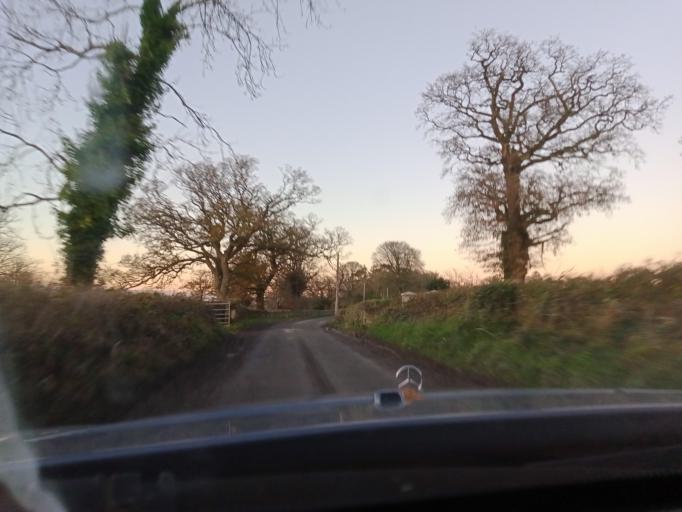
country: IE
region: Leinster
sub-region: Kilkenny
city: Thomastown
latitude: 52.4607
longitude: -7.1020
